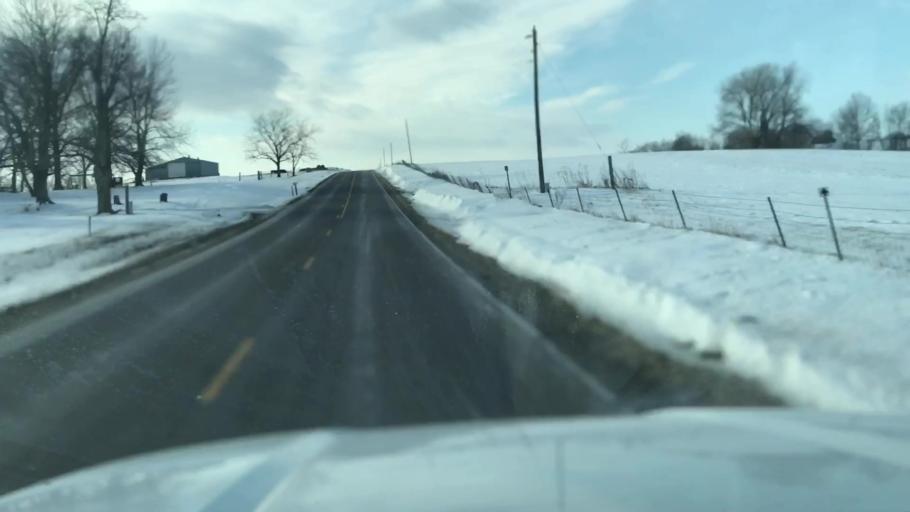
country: US
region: Missouri
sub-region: Nodaway County
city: Maryville
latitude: 40.2009
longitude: -94.8982
